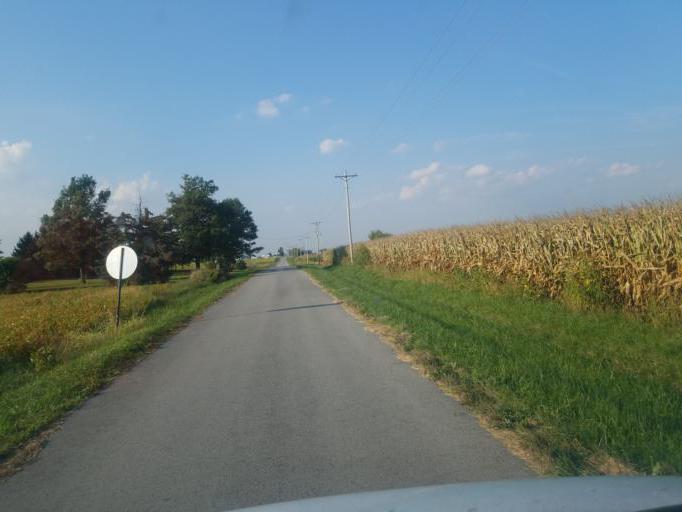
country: US
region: Ohio
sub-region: Seneca County
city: Tiffin
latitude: 40.9589
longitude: -83.1126
